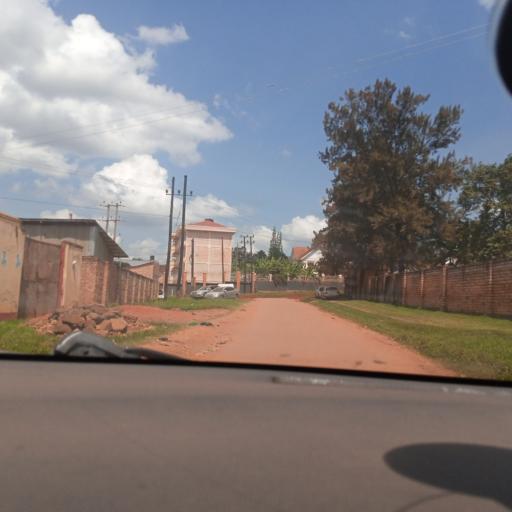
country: UG
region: Central Region
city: Masaka
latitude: -0.3312
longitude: 31.7413
